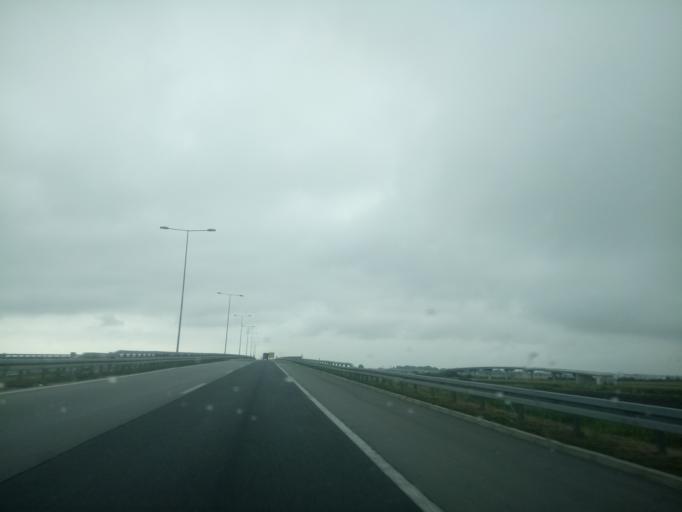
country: RS
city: Novi Banovci
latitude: 44.8875
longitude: 20.2836
